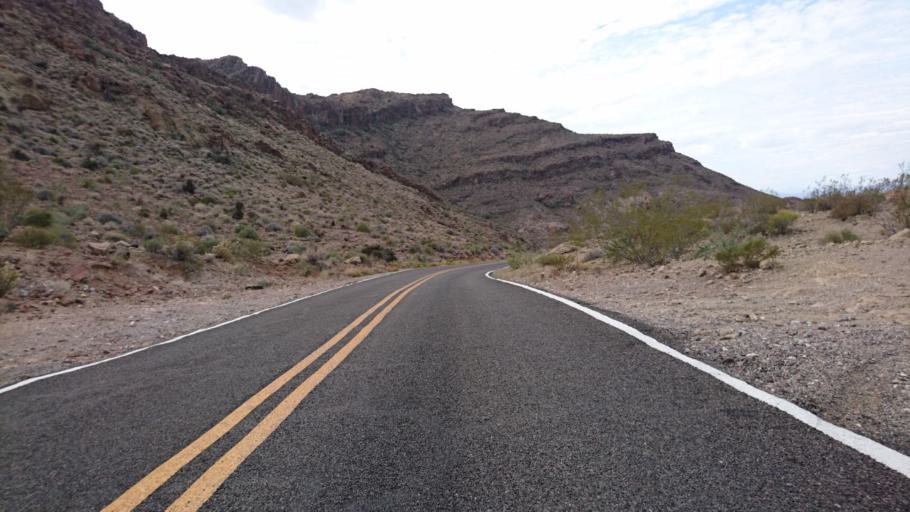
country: US
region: Arizona
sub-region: Mohave County
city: Bullhead City
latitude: 35.0428
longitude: -114.3691
